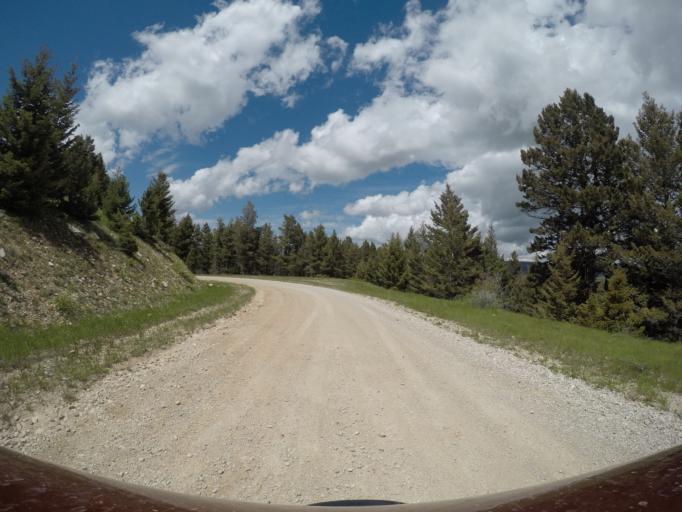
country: US
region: Wyoming
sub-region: Big Horn County
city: Lovell
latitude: 45.1926
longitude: -108.4800
